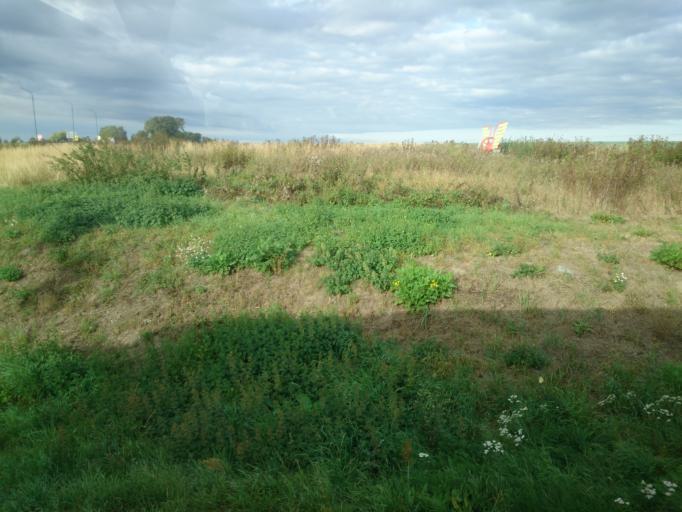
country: DE
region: Mecklenburg-Vorpommern
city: Pasewalk
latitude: 53.5155
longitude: 13.9779
